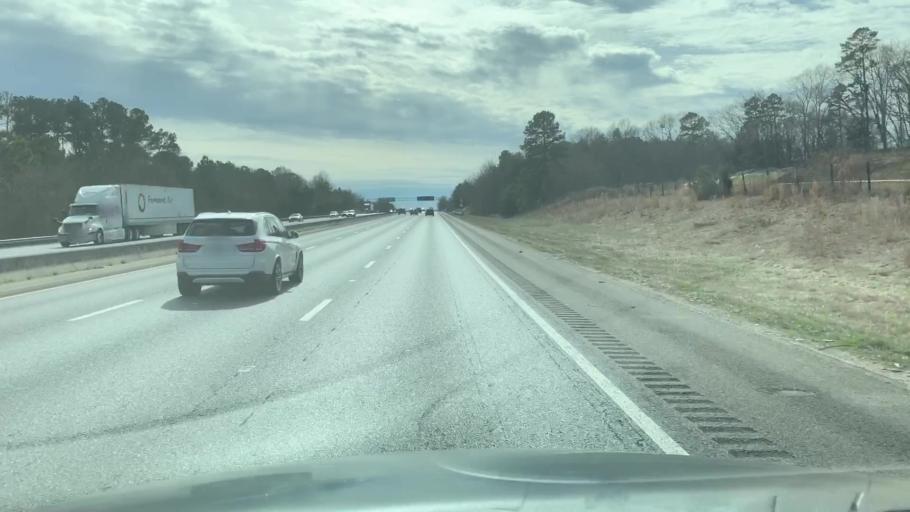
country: US
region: South Carolina
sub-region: Greenville County
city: Golden Grove
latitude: 34.7552
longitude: -82.4772
